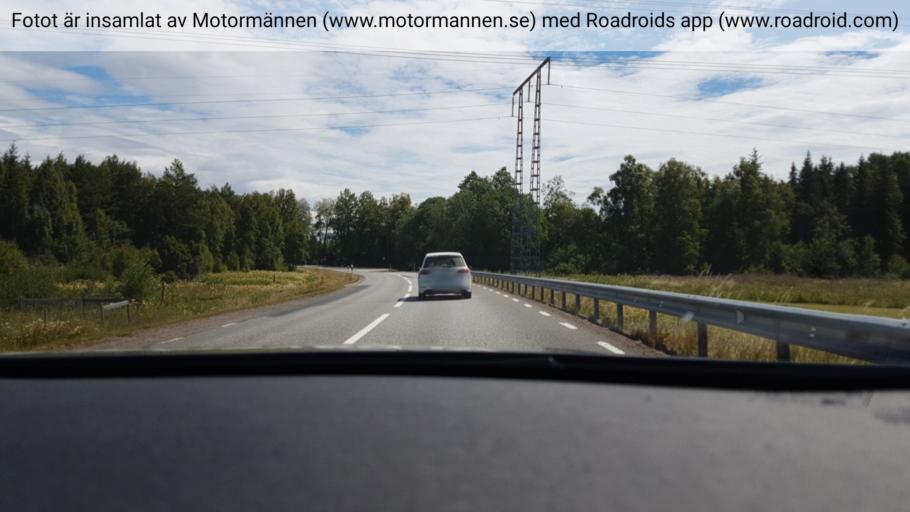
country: SE
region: Joenkoeping
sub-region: Aneby Kommun
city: Aneby
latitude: 57.9755
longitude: 14.7723
